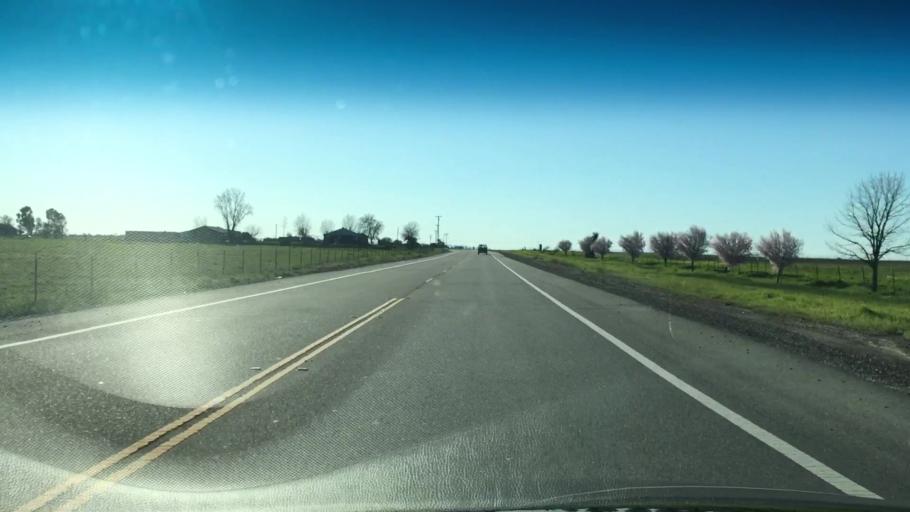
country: US
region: California
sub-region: Sacramento County
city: Wilton
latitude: 38.4965
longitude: -121.2552
